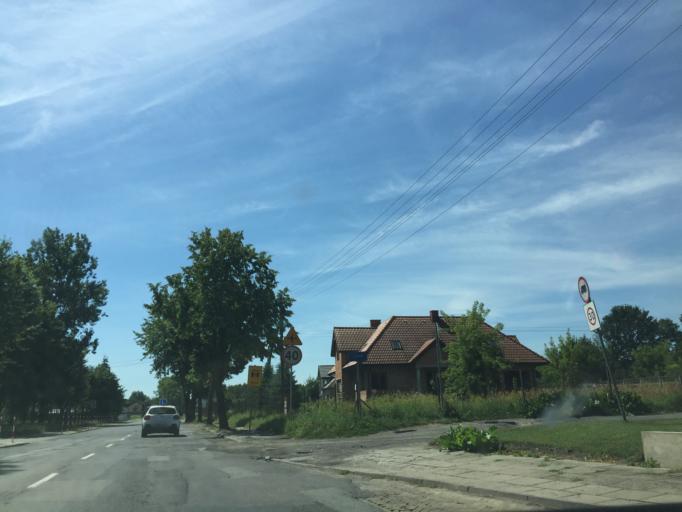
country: PL
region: Lodz Voivodeship
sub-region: Piotrkow Trybunalski
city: Piotrkow Trybunalski
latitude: 51.4188
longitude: 19.7129
